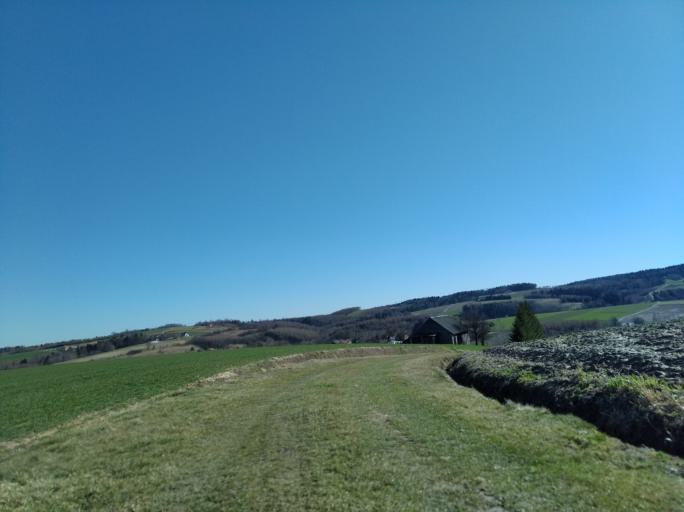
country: PL
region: Subcarpathian Voivodeship
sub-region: Powiat strzyzowski
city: Wisniowa
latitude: 49.9138
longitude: 21.6862
